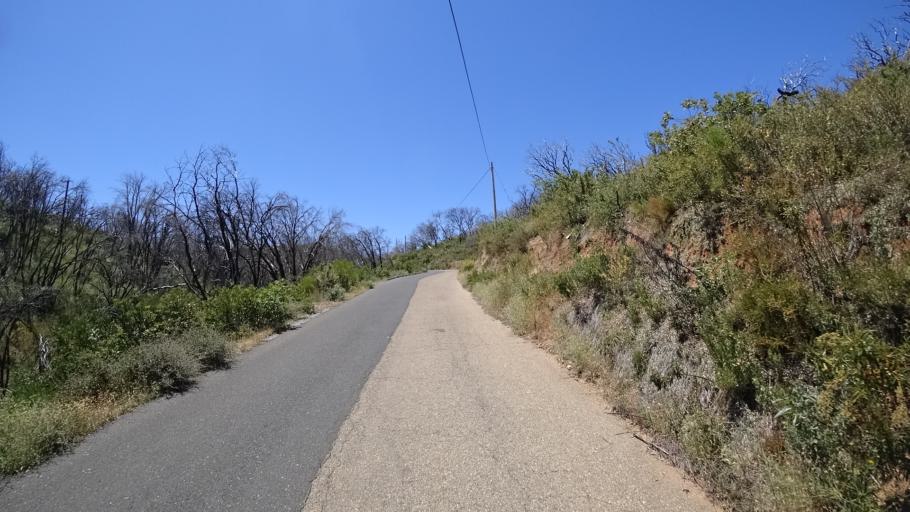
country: US
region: California
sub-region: Calaveras County
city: Mountain Ranch
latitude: 38.2293
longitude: -120.5904
